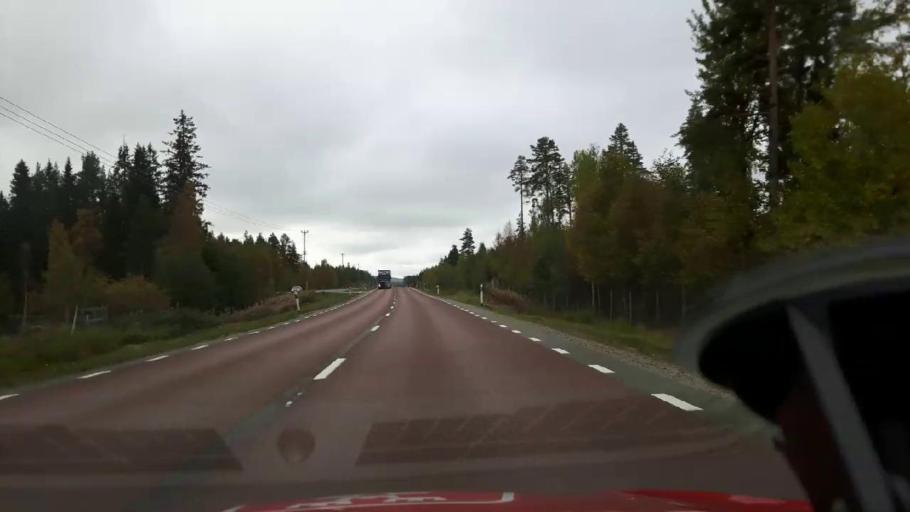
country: SE
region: Jaemtland
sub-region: Harjedalens Kommun
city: Sveg
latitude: 62.2413
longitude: 14.8298
